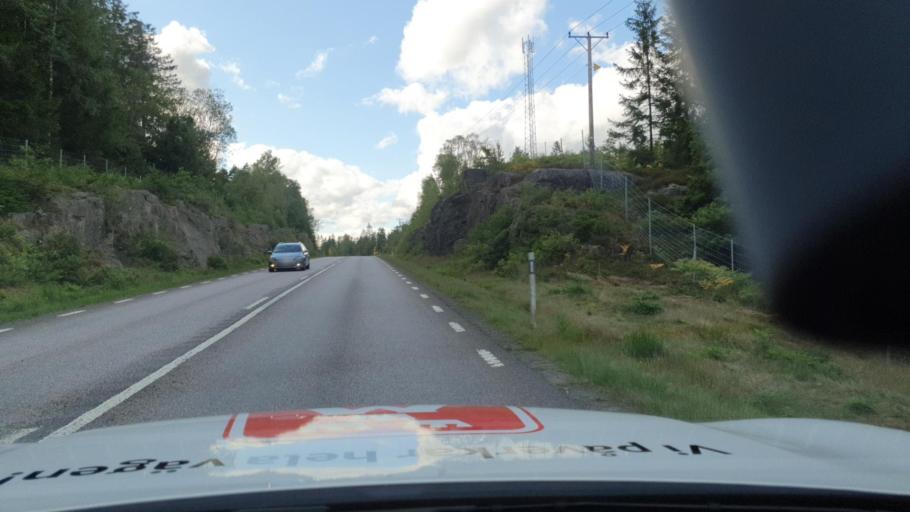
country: SE
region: Vaestra Goetaland
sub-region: Harryda Kommun
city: Hindas
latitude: 57.6495
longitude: 12.4016
